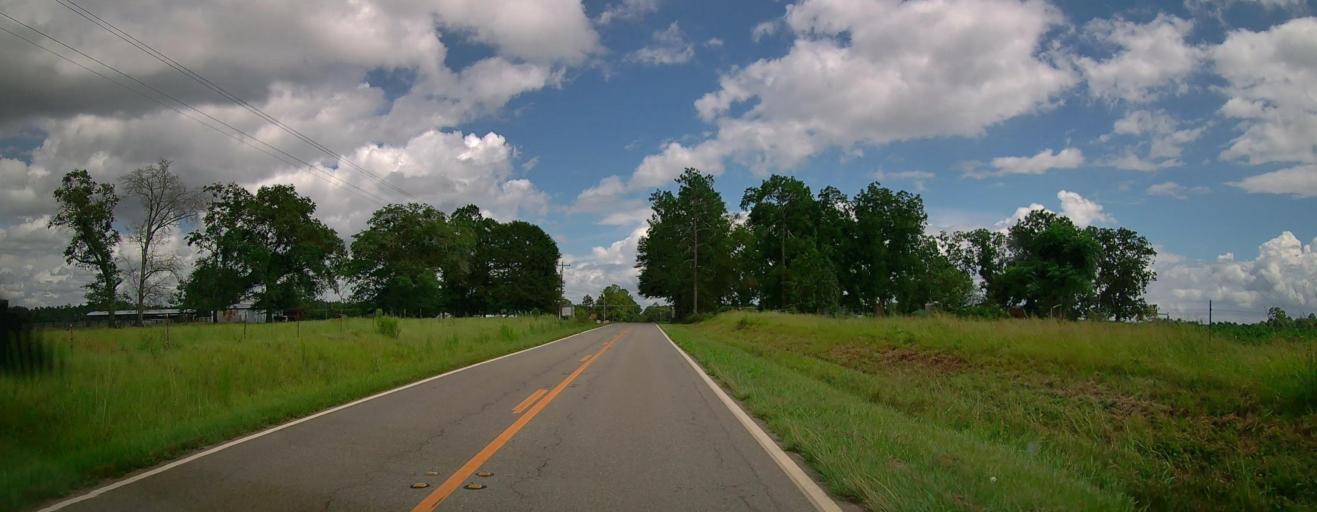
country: US
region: Georgia
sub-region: Ben Hill County
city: Fitzgerald
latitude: 31.6851
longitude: -83.2092
